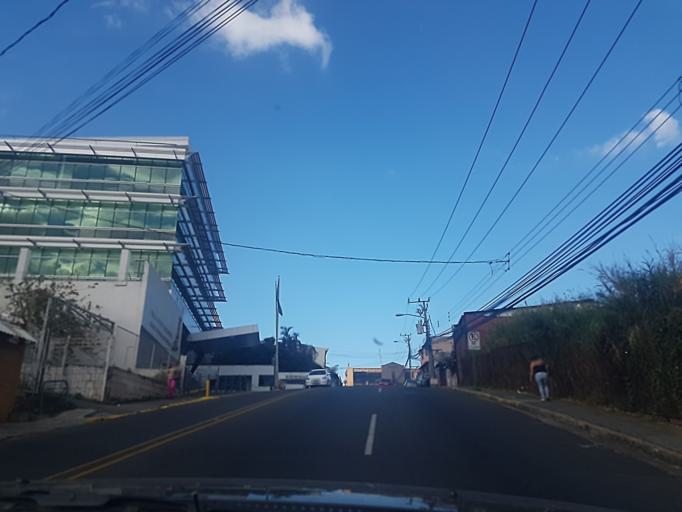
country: CR
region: San Jose
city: San Jose
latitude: 9.9279
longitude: -84.1042
